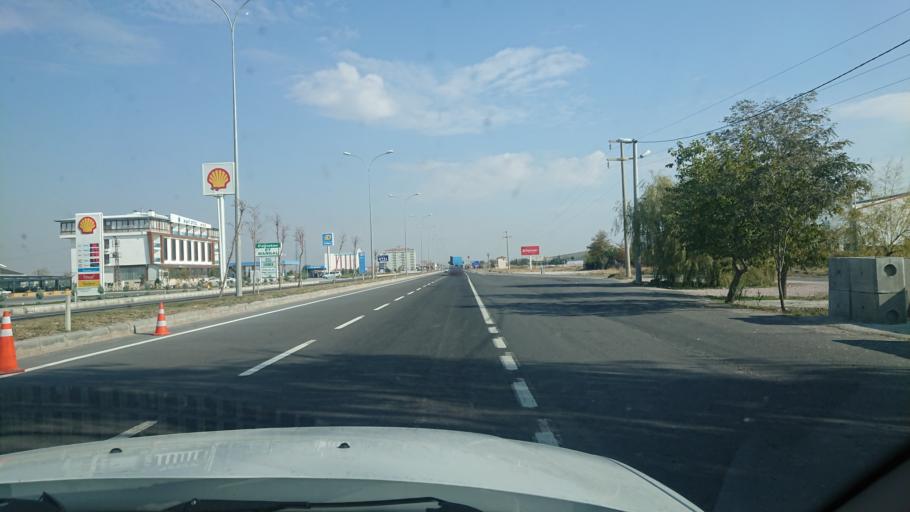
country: TR
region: Aksaray
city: Aksaray
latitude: 38.3470
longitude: 33.9567
